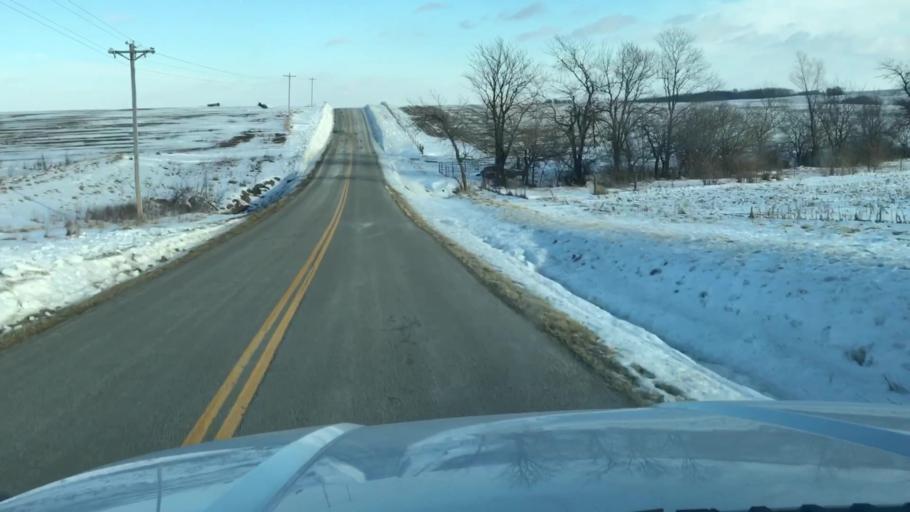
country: US
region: Missouri
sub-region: Holt County
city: Oregon
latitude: 40.1006
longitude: -94.9878
